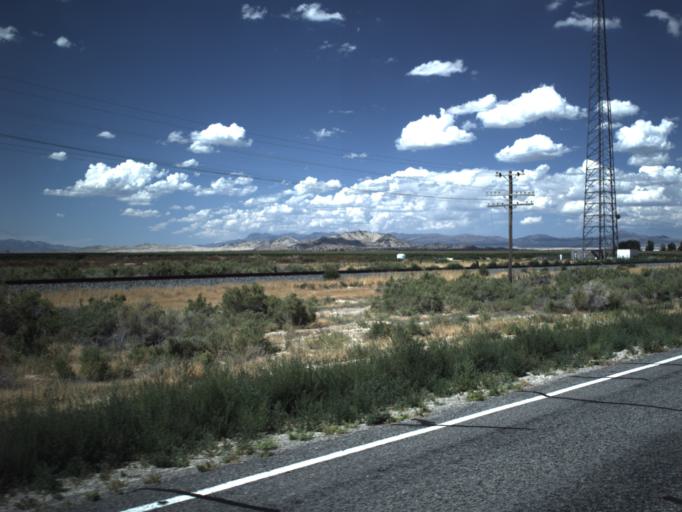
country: US
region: Utah
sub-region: Millard County
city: Delta
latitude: 39.5286
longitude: -112.3708
